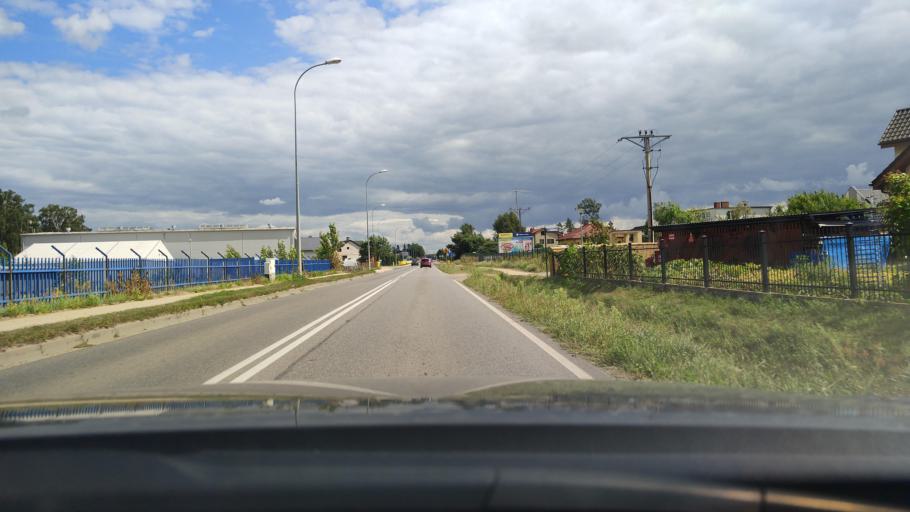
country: PL
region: Pomeranian Voivodeship
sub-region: Powiat wejherowski
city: Bojano
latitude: 54.4776
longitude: 18.3655
